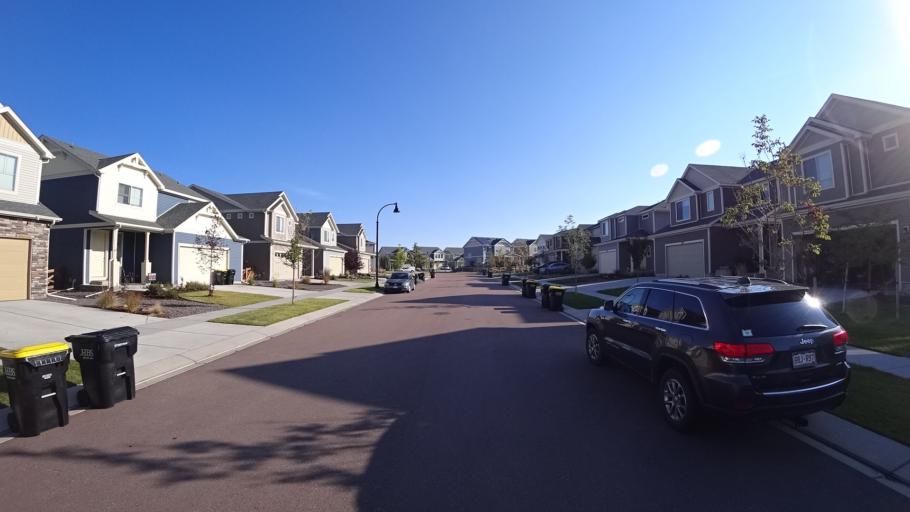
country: US
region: Colorado
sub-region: El Paso County
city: Cimarron Hills
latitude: 38.9349
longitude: -104.6586
